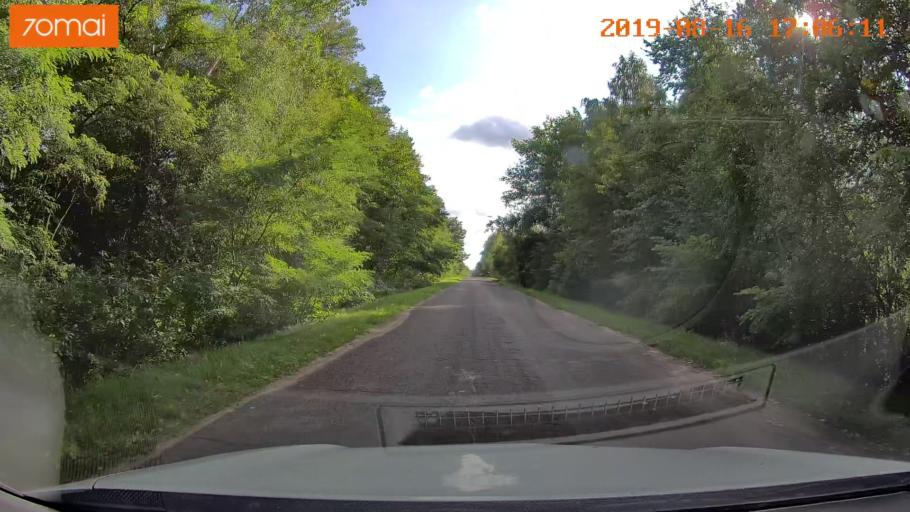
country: BY
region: Mogilev
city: Hlusha
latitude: 53.2296
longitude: 28.9360
